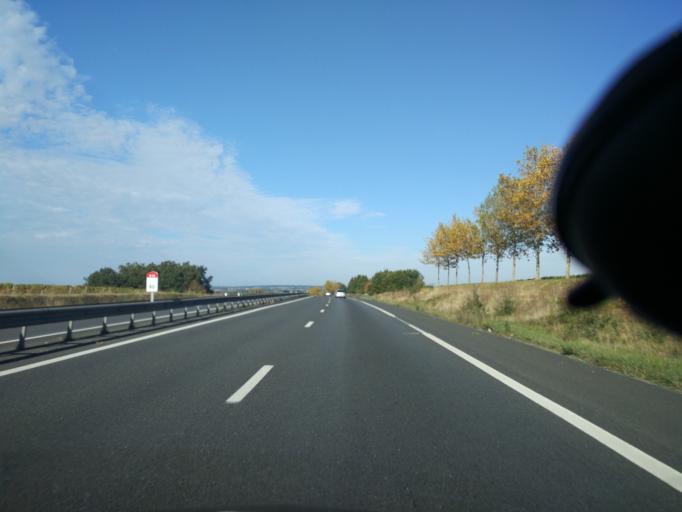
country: FR
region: Poitou-Charentes
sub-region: Departement de la Charente
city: Barbezieux-Saint-Hilaire
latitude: 45.4795
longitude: -0.1312
